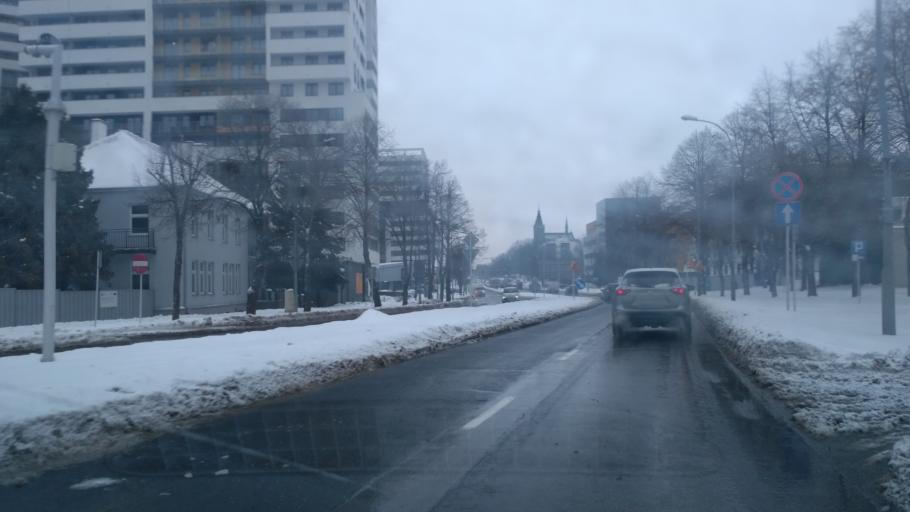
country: PL
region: Subcarpathian Voivodeship
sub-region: Rzeszow
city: Rzeszow
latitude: 50.0483
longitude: 21.9998
